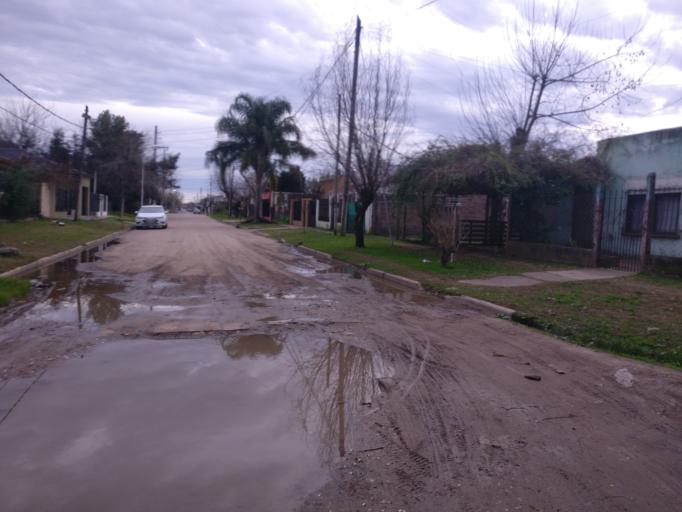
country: AR
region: Buenos Aires
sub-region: Partido de Ezeiza
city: Ezeiza
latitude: -34.9383
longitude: -58.6140
